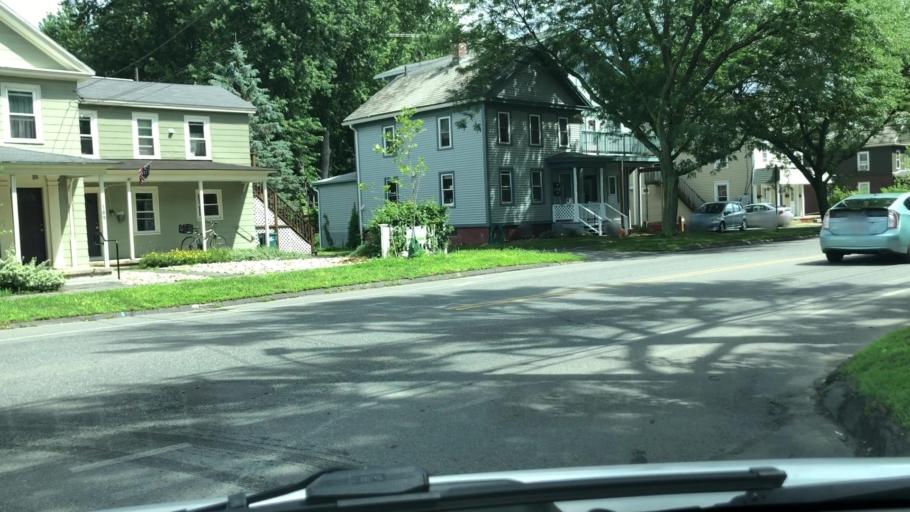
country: US
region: Massachusetts
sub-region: Hampshire County
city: Northampton
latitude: 42.3263
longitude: -72.6253
